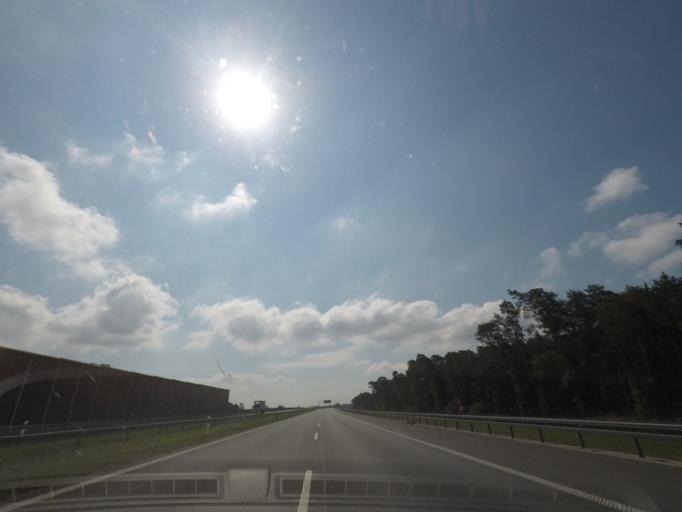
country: PL
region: Kujawsko-Pomorskie
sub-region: Powiat aleksandrowski
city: Ciechocinek
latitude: 52.8765
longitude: 18.7469
